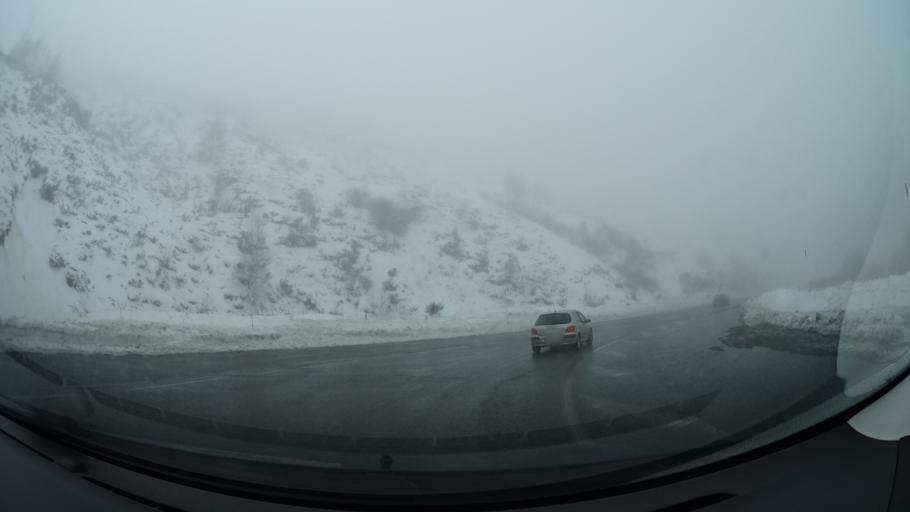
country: AD
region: Encamp
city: Pas de la Casa
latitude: 42.5762
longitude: 1.7892
